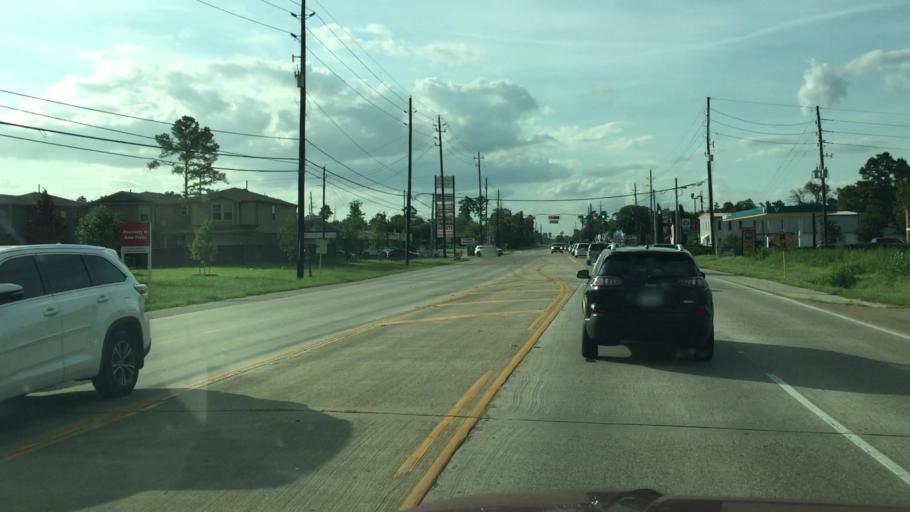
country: US
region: Texas
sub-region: Harris County
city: Hudson
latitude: 29.9980
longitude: -95.5058
